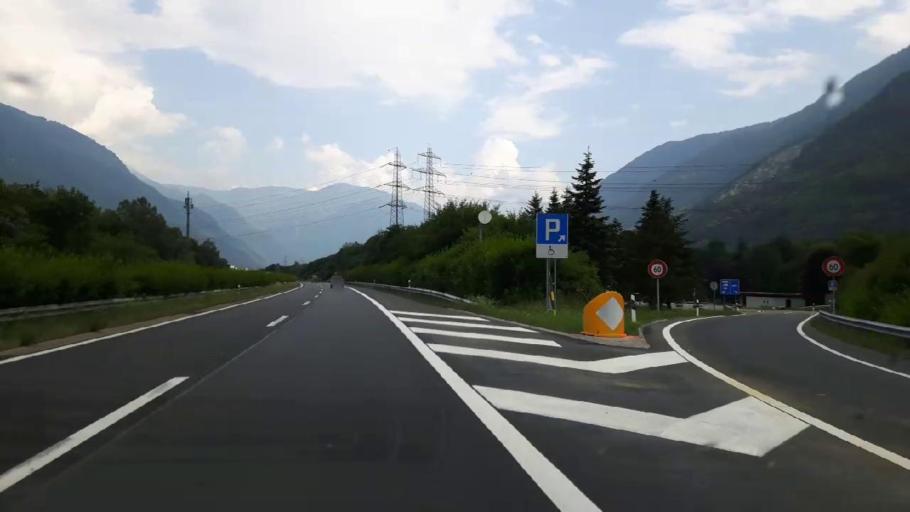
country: CH
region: Ticino
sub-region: Riviera District
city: Claro
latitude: 46.2744
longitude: 8.9975
